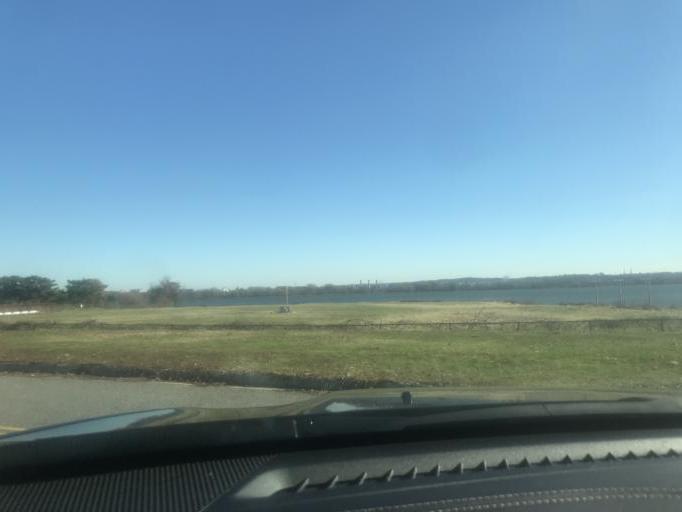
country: US
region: Washington, D.C.
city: Washington, D.C.
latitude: 38.8642
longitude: -77.0404
